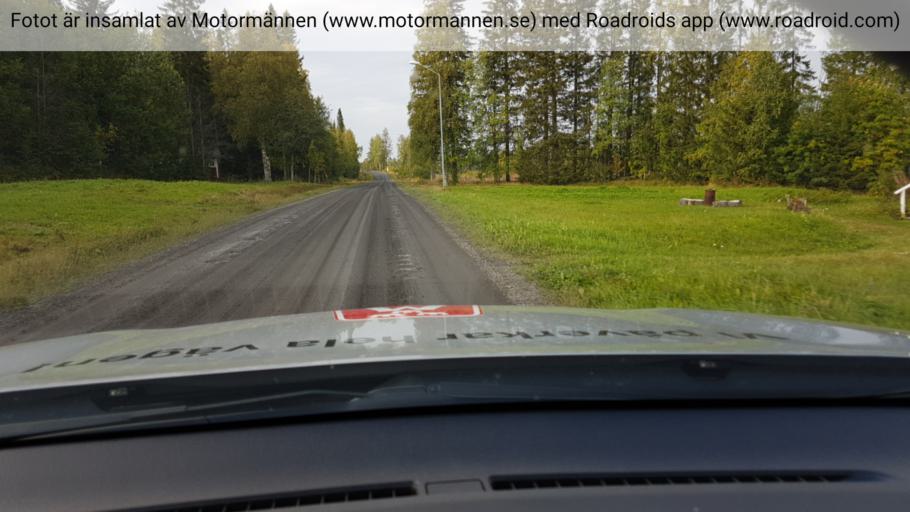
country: SE
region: Jaemtland
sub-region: Stroemsunds Kommun
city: Stroemsund
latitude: 64.1184
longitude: 15.8086
